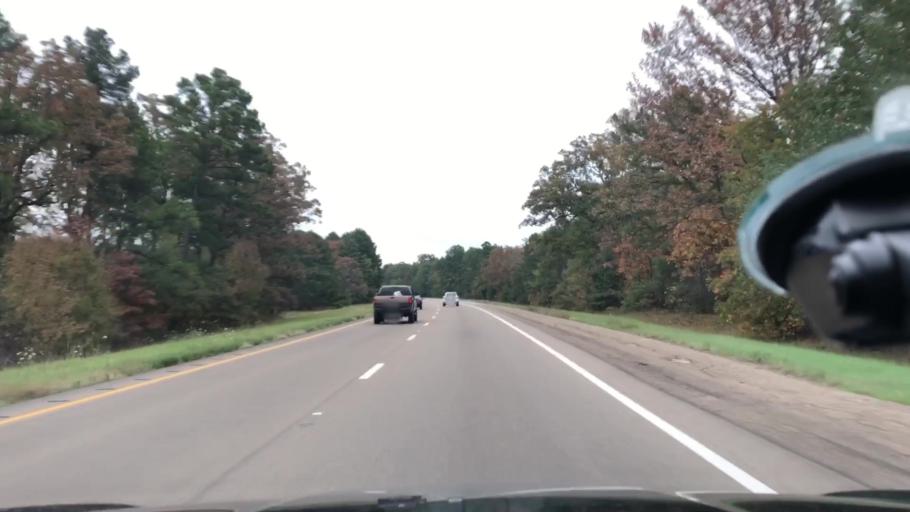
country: US
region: Texas
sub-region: Morris County
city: Naples
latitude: 33.2965
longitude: -94.7186
